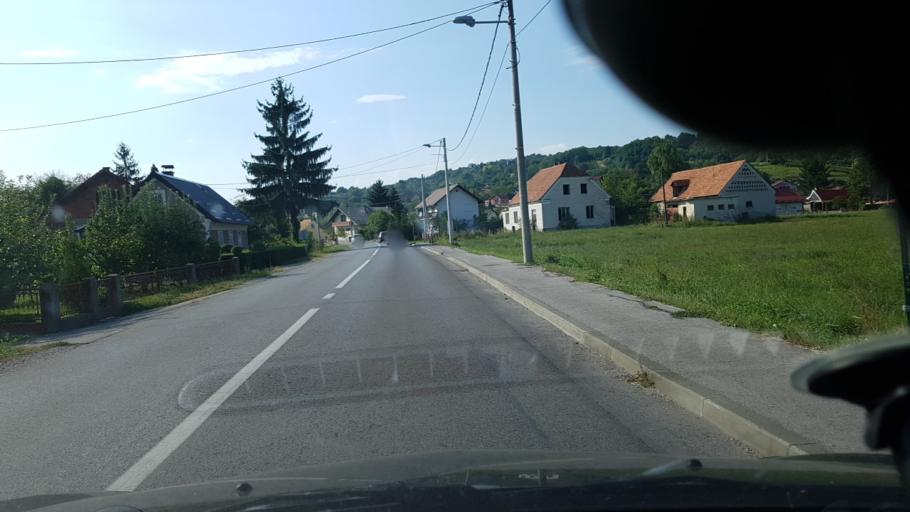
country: HR
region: Zagrebacka
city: Bregana
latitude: 45.8818
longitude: 15.7235
